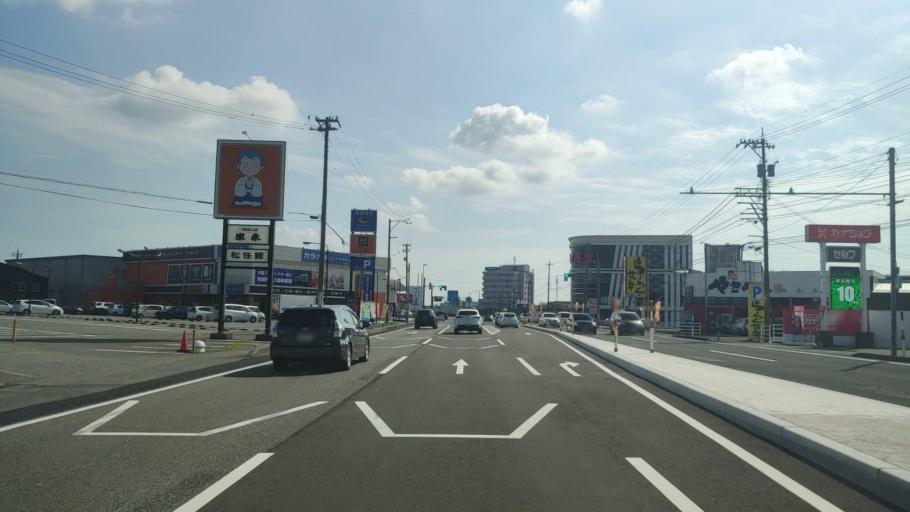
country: JP
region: Ishikawa
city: Matsuto
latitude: 36.5278
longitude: 136.5890
